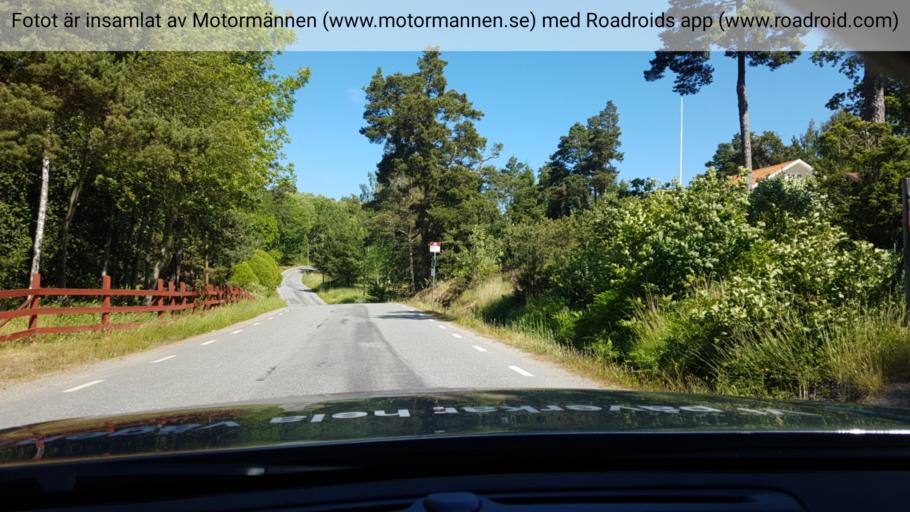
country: SE
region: Stockholm
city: Dalaro
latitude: 59.1575
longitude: 18.4395
